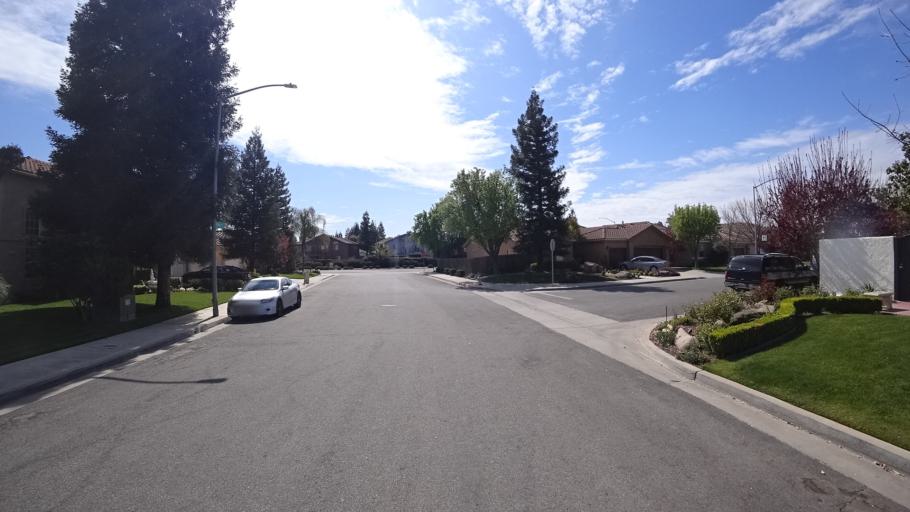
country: US
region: California
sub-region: Fresno County
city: Biola
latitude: 36.8491
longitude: -119.8984
